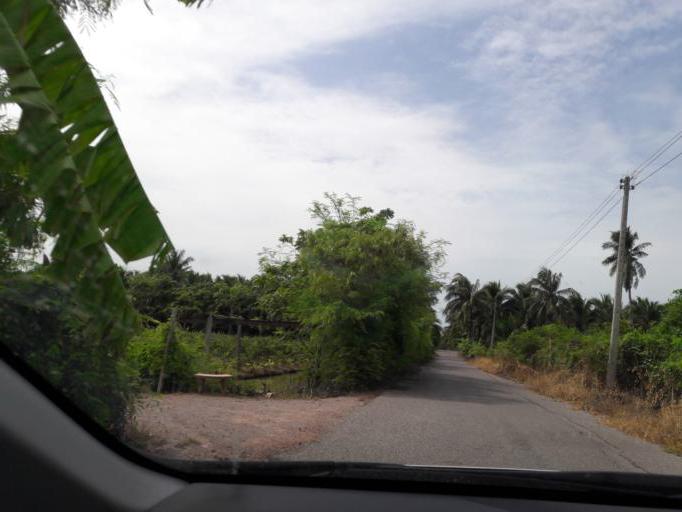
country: TH
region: Ratchaburi
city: Damnoen Saduak
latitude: 13.5267
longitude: 99.9936
